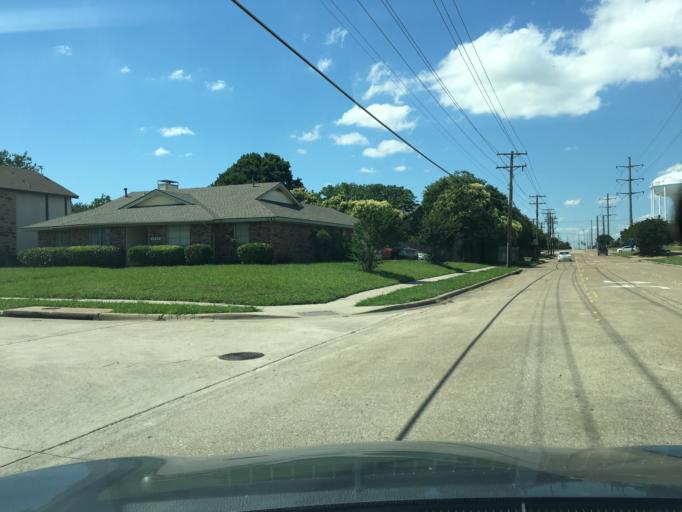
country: US
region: Texas
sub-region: Dallas County
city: Richardson
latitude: 32.9519
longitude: -96.7053
